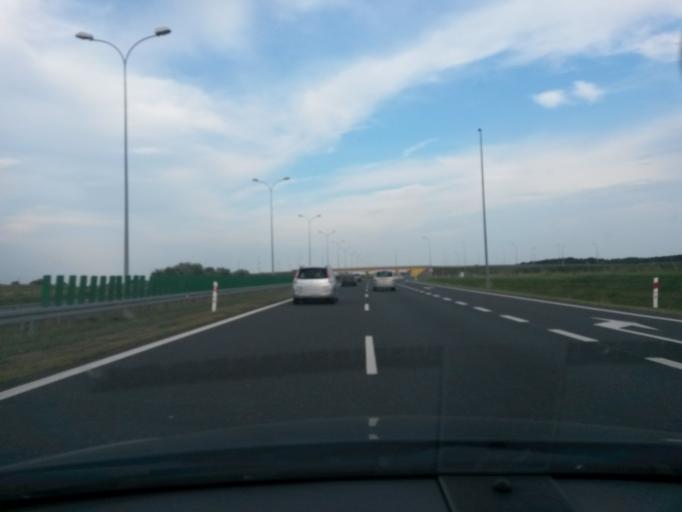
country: PL
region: Lodz Voivodeship
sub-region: Powiat poddebicki
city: Wartkowice
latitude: 51.9956
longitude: 19.0344
